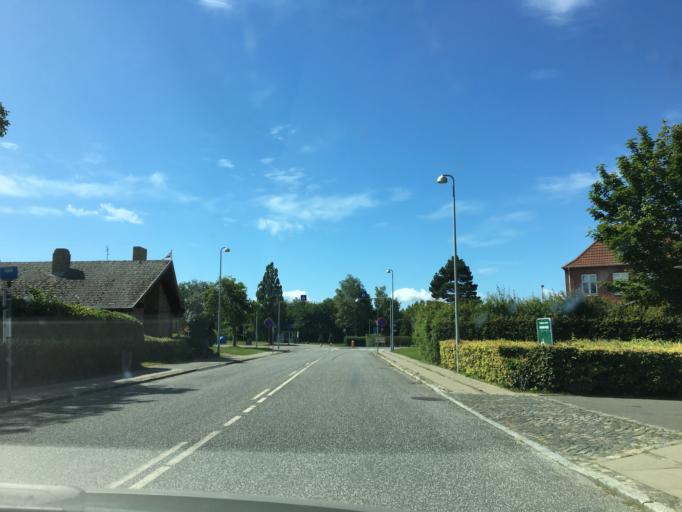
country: DK
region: South Denmark
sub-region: Langeland Kommune
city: Rudkobing
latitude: 54.9340
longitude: 10.7207
